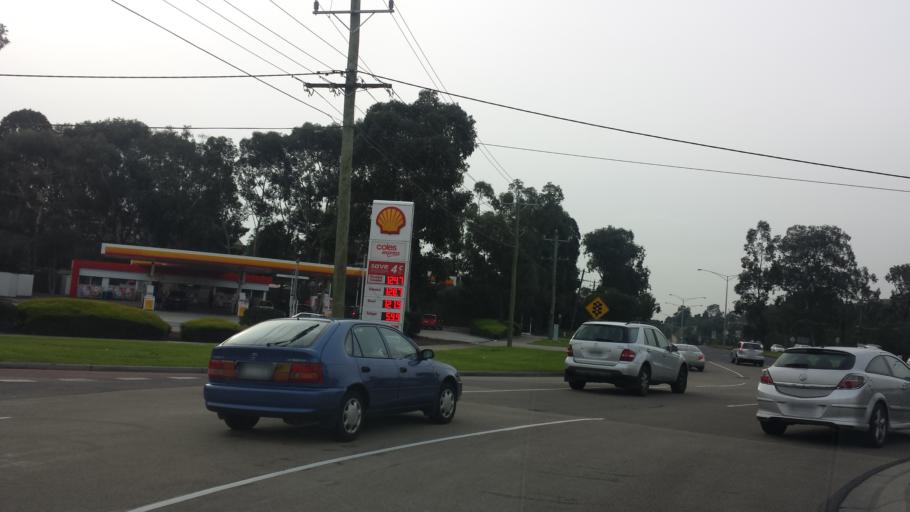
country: AU
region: Victoria
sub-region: Banyule
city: Darch
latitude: -37.7526
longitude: 145.1348
